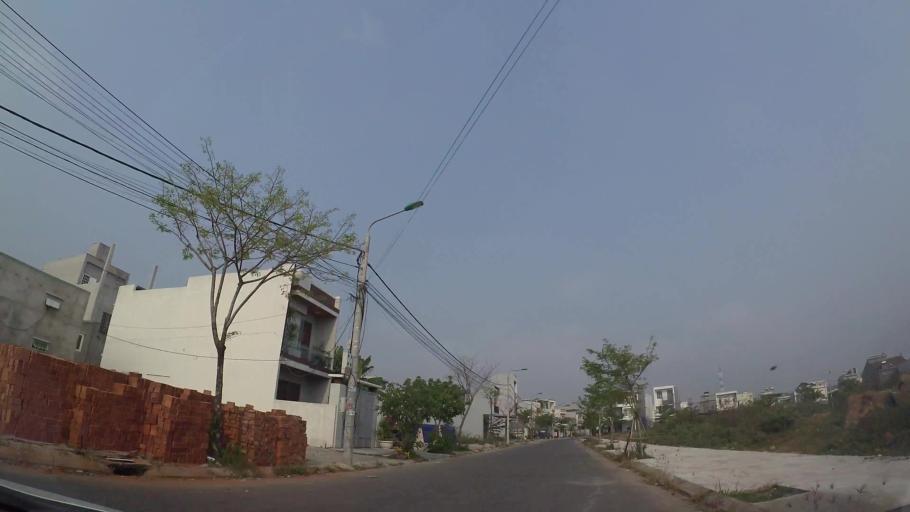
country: VN
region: Da Nang
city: Cam Le
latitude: 16.0074
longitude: 108.2248
